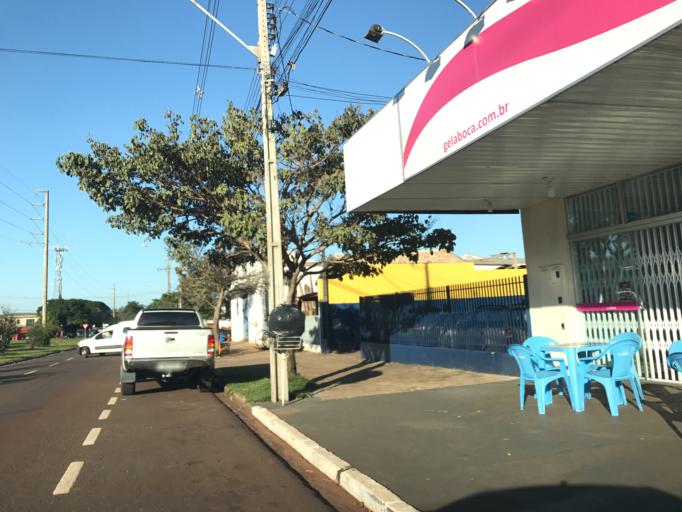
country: BR
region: Parana
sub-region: Maringa
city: Maringa
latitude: -23.4497
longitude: -51.9556
